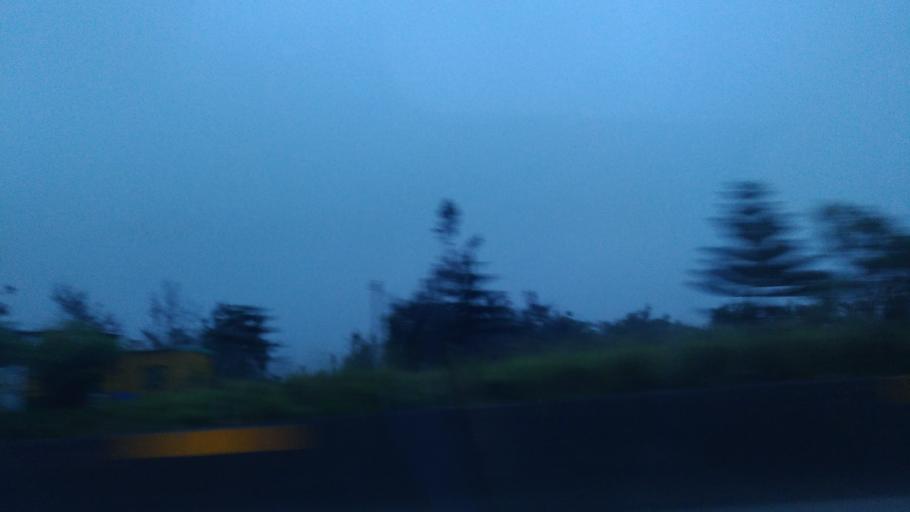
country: TW
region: Taiwan
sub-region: Miaoli
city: Miaoli
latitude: 24.5977
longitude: 120.7420
